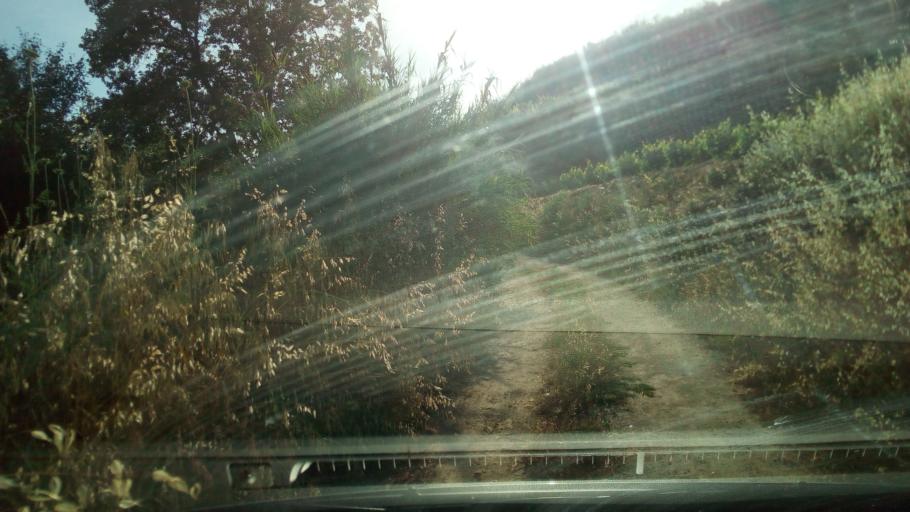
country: CY
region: Pafos
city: Tala
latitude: 34.8724
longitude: 32.4780
